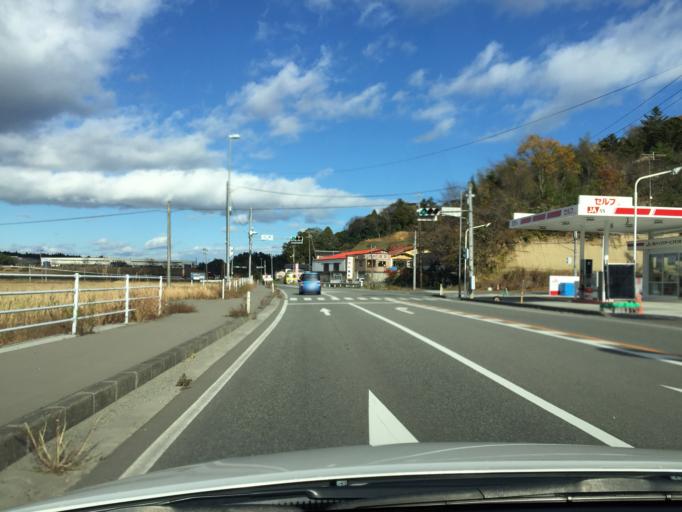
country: JP
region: Fukushima
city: Namie
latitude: 37.5419
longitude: 141.0077
